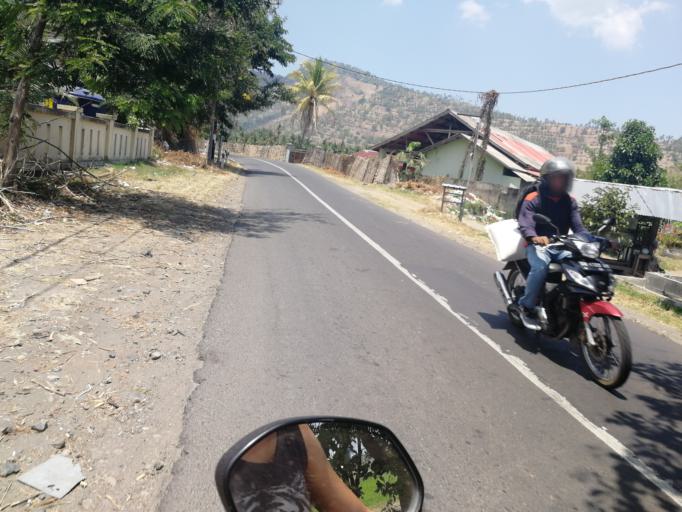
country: ID
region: West Nusa Tenggara
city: Karangsubagan
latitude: -8.4092
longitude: 116.1003
